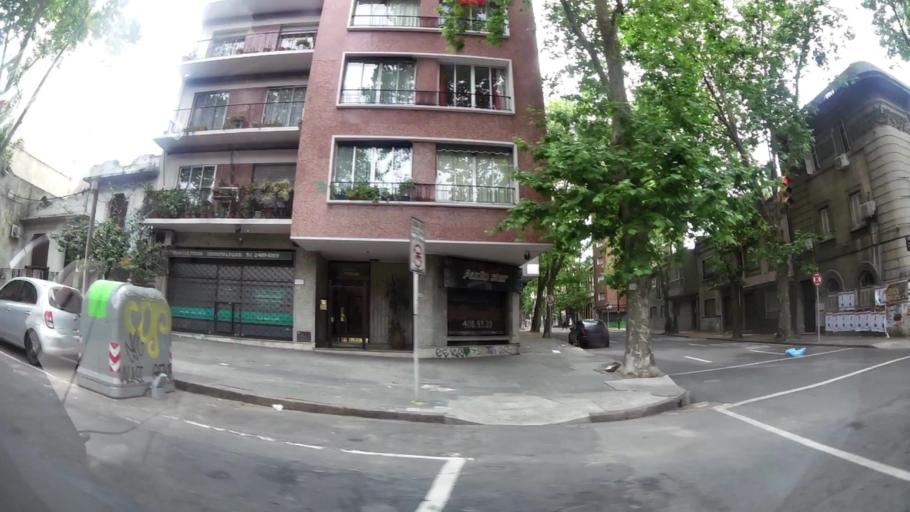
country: UY
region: Montevideo
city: Montevideo
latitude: -34.9033
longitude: -56.1737
